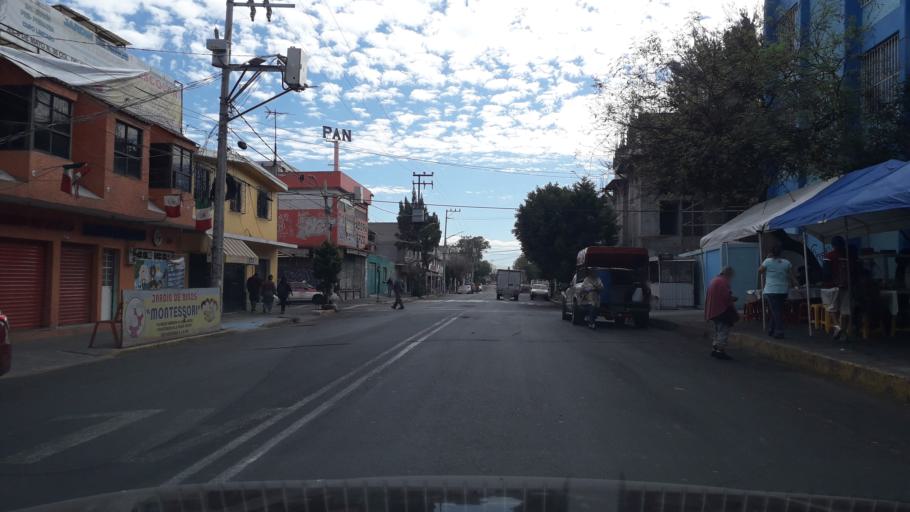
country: MX
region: Mexico City
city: Gustavo A. Madero
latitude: 19.4984
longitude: -99.0924
